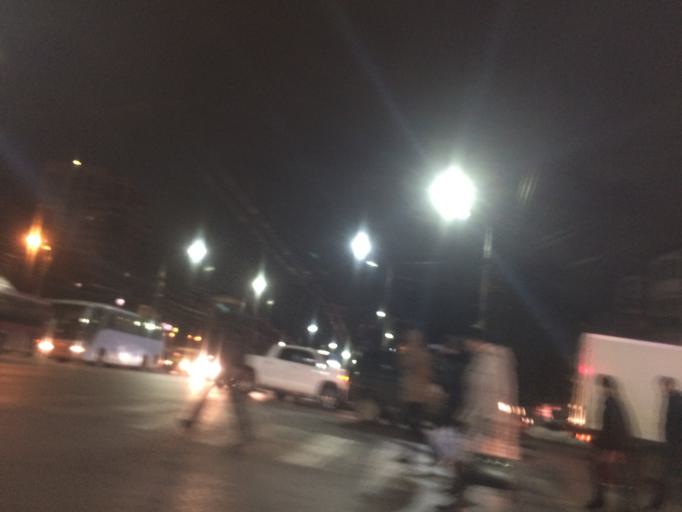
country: RU
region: Tula
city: Mendeleyevskiy
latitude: 54.1642
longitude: 37.5868
